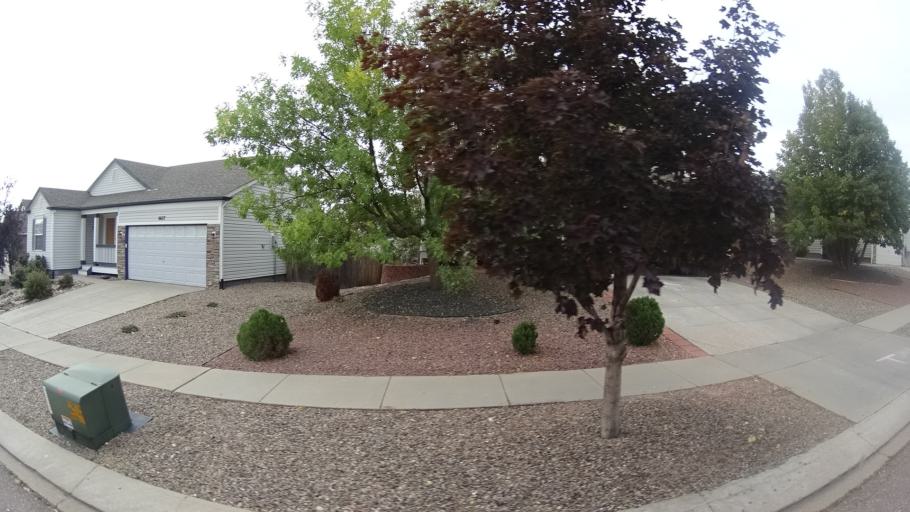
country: US
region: Colorado
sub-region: El Paso County
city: Cimarron Hills
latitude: 38.9162
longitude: -104.7020
